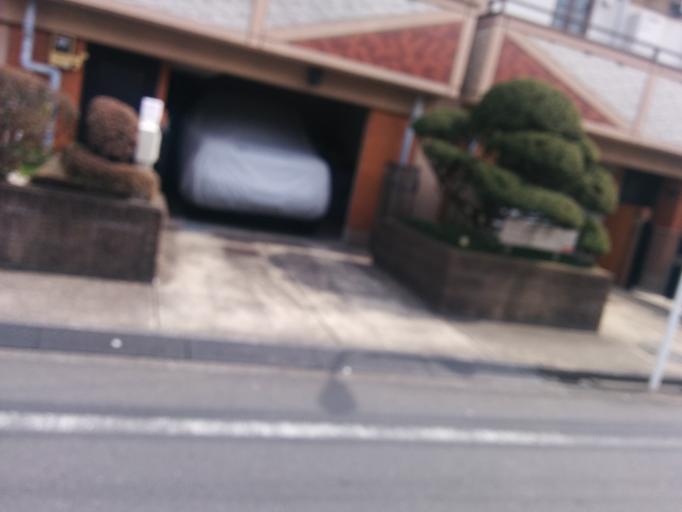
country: JP
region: Tokyo
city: Tokyo
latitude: 35.6850
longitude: 139.6457
